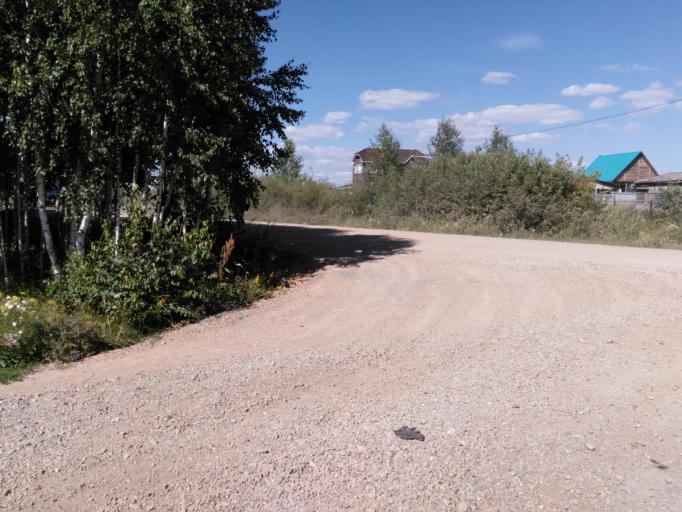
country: RU
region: Bashkortostan
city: Uchaly
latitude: 54.2911
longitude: 59.3687
